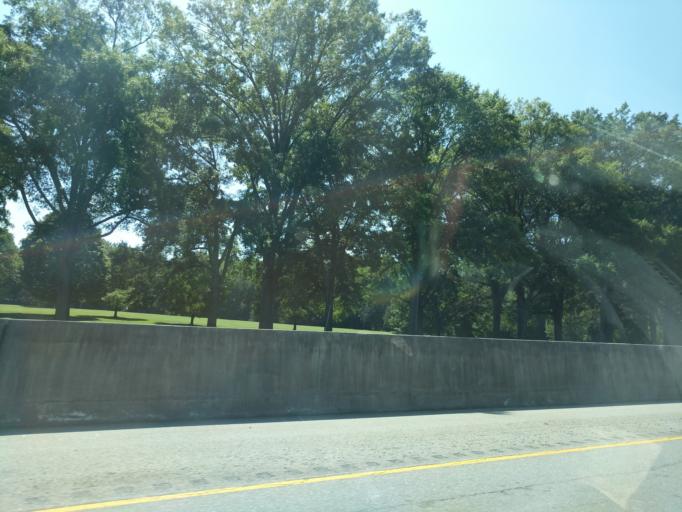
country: US
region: South Carolina
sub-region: Spartanburg County
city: Valley Falls
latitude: 34.9914
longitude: -81.9609
